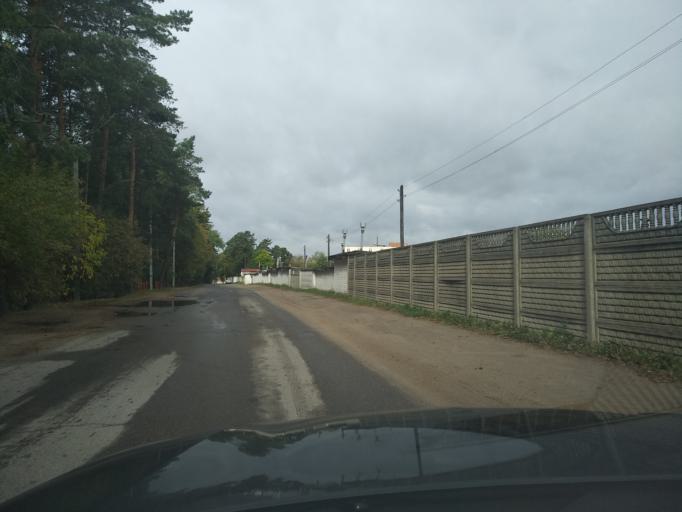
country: BY
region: Minsk
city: Minsk
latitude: 53.8792
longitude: 27.6413
